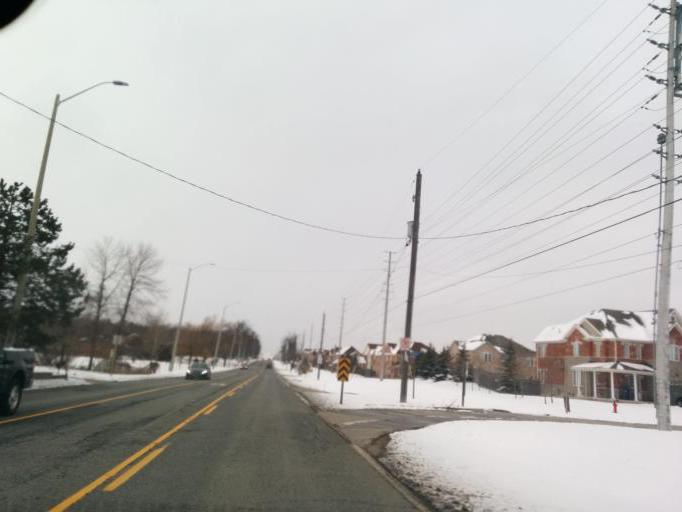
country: CA
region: Ontario
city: Mississauga
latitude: 43.5359
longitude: -79.7344
